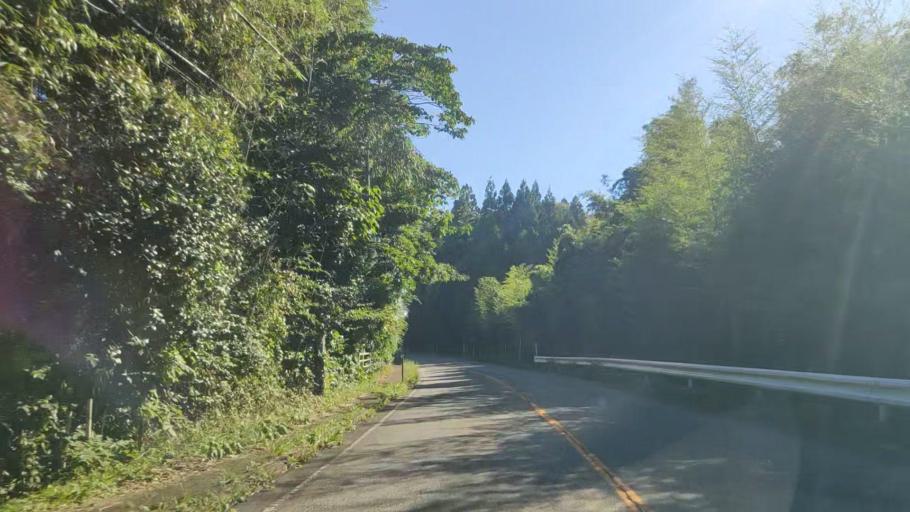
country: JP
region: Ishikawa
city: Nanao
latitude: 37.2618
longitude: 137.0890
